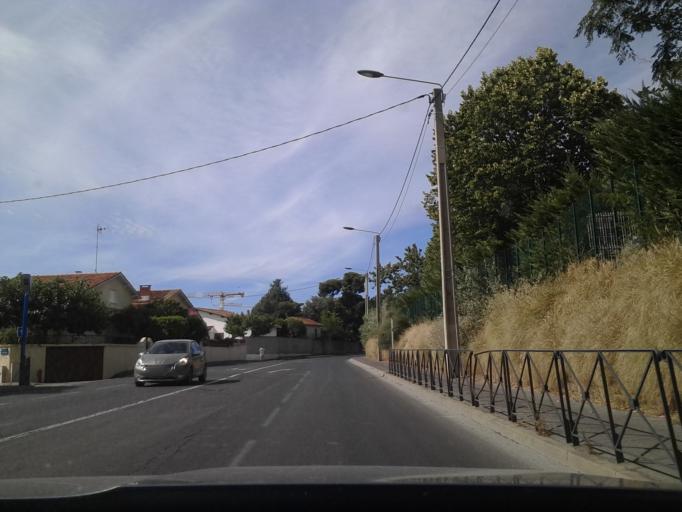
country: FR
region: Languedoc-Roussillon
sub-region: Departement de l'Herault
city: Montpellier
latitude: 43.5971
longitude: 3.8926
